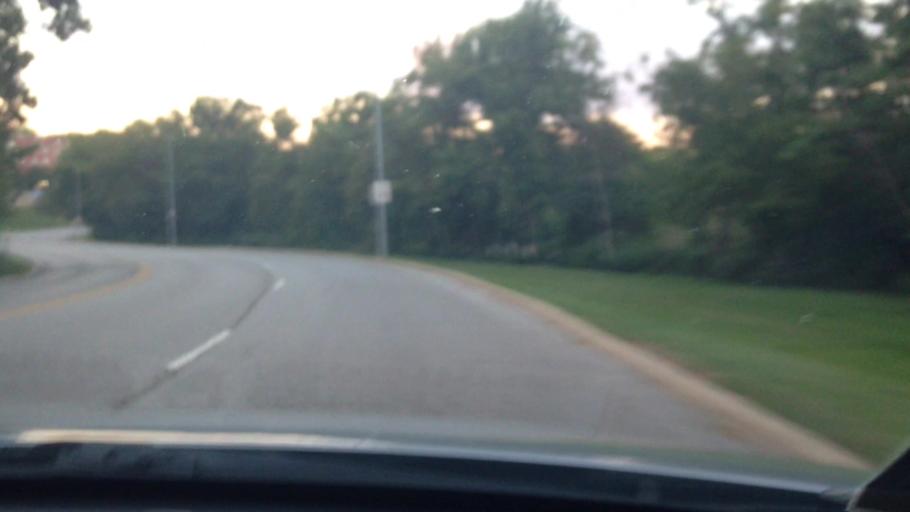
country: US
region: Kansas
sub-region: Johnson County
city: Westwood
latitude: 39.0470
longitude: -94.5789
